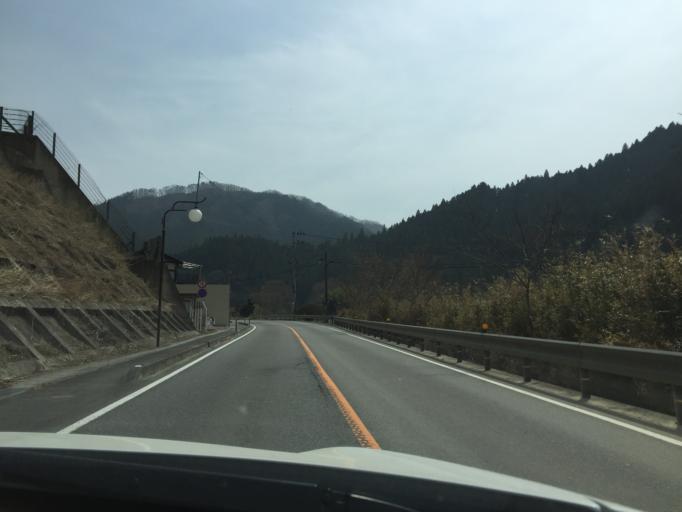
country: JP
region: Fukushima
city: Ishikawa
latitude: 37.0600
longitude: 140.5839
